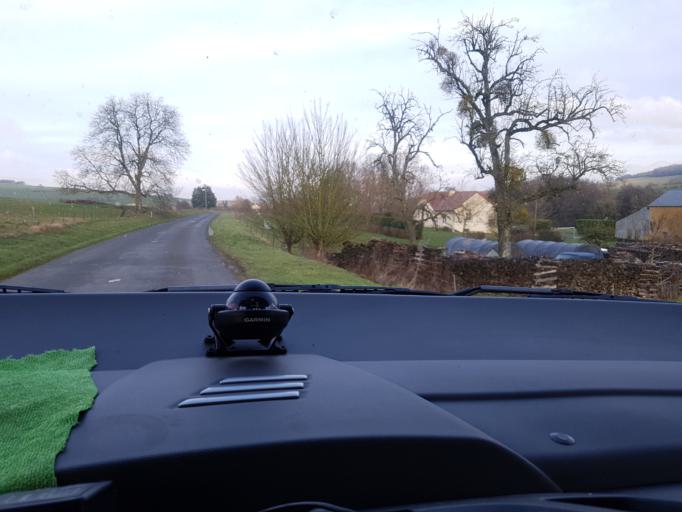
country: FR
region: Champagne-Ardenne
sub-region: Departement des Ardennes
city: Tournes
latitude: 49.7440
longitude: 4.6005
